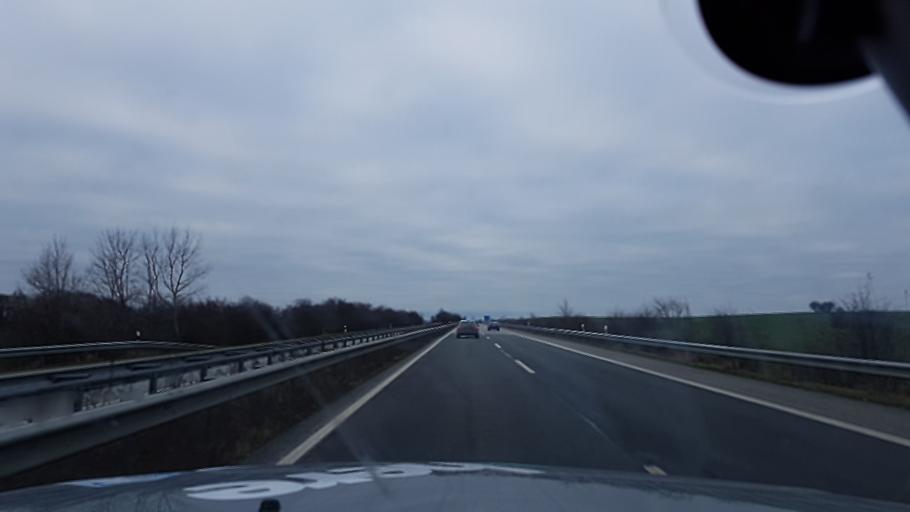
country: DE
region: Schleswig-Holstein
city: Gremersdorf
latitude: 54.3206
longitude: 10.9251
